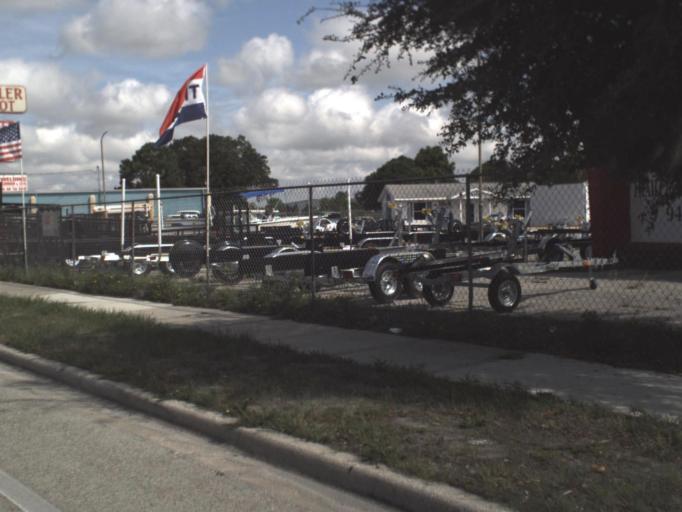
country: US
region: Florida
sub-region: Manatee County
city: Whitfield
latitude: 27.3909
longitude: -82.5601
